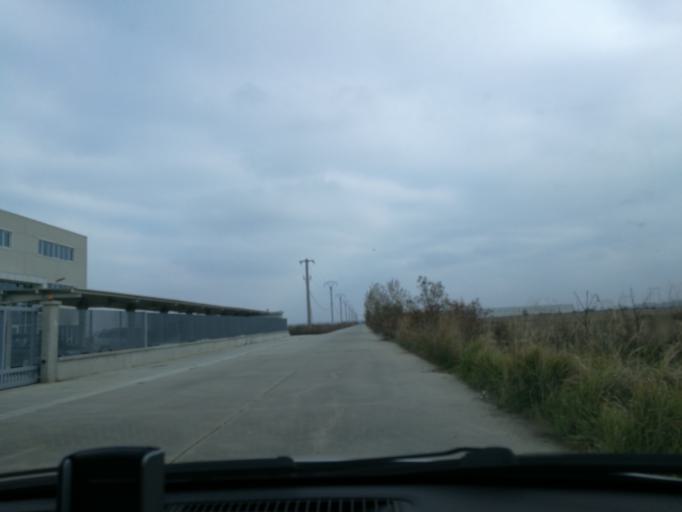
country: RO
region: Giurgiu
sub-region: Comuna Bolintin Deal
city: Bolintin Deal
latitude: 44.4625
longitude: 25.8456
